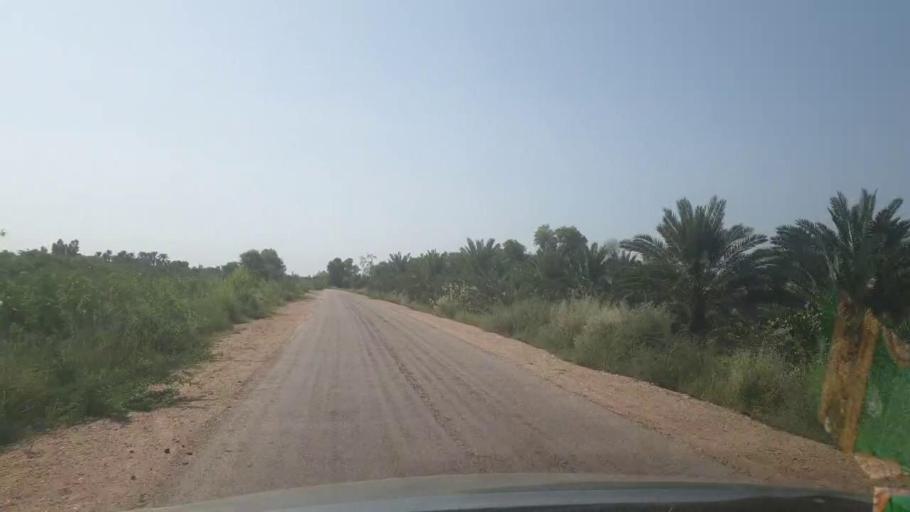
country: PK
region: Sindh
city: Rohri
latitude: 27.4627
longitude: 69.0412
